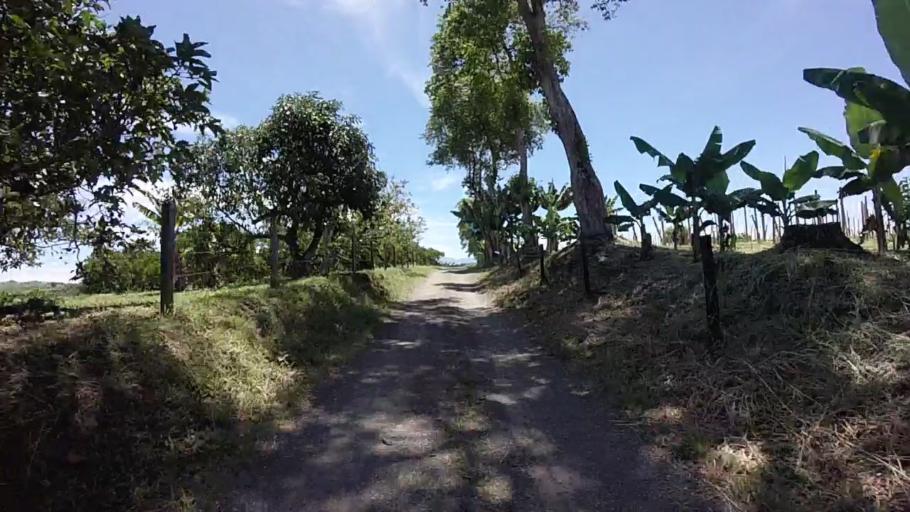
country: CO
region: Valle del Cauca
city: Alcala
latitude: 4.7055
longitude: -75.8188
